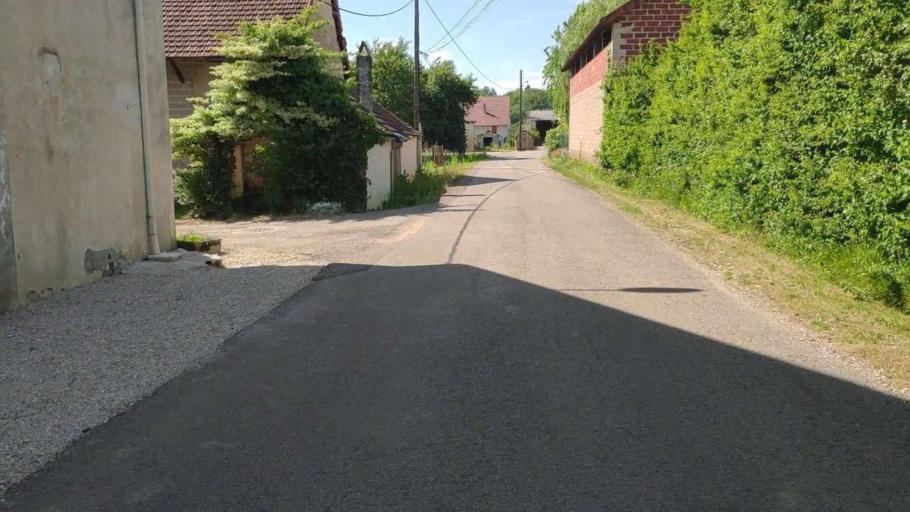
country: FR
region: Franche-Comte
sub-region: Departement du Jura
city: Bletterans
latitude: 46.7647
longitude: 5.4764
